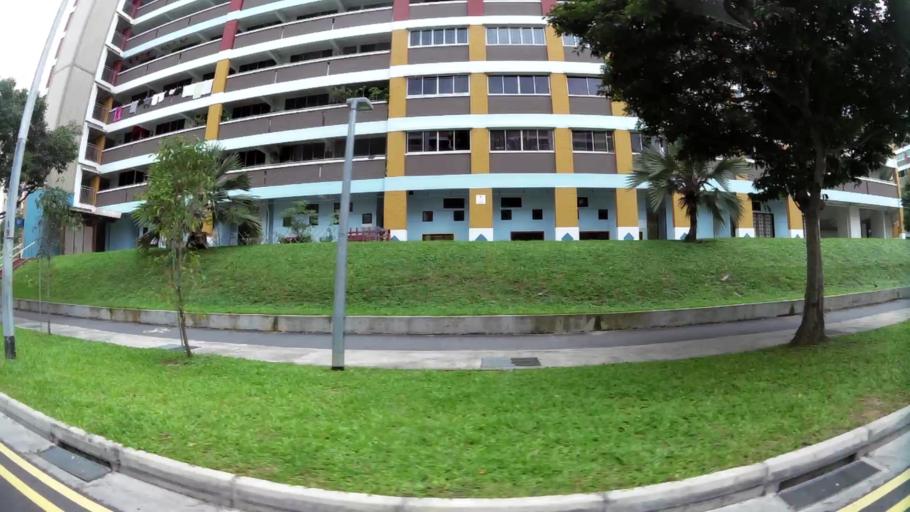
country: SG
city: Singapore
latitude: 1.3506
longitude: 103.9320
